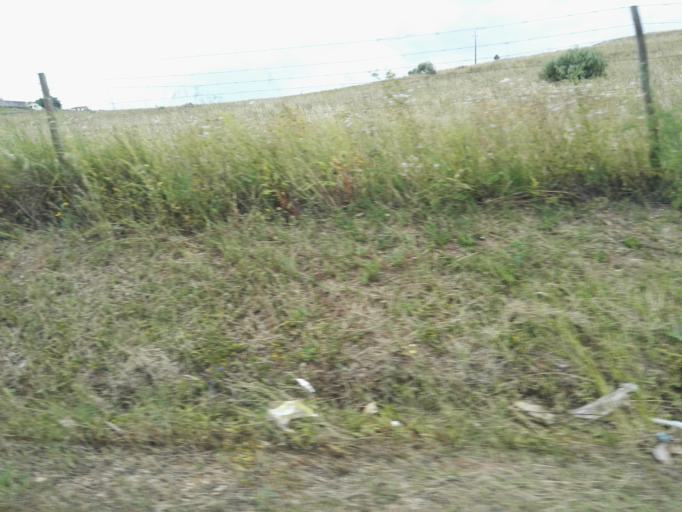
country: PT
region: Portalegre
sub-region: Elvas
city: Elvas
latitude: 38.8734
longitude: -7.1550
